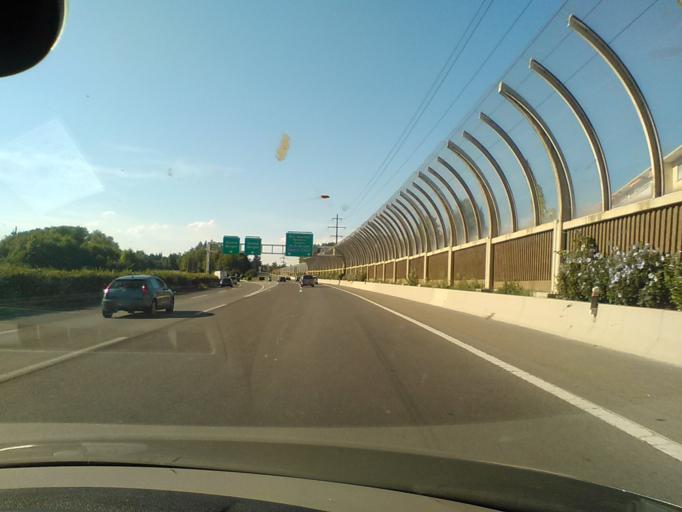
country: CH
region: Vaud
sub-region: Ouest Lausannois District
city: Chavannes
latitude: 46.5375
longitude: 6.5704
